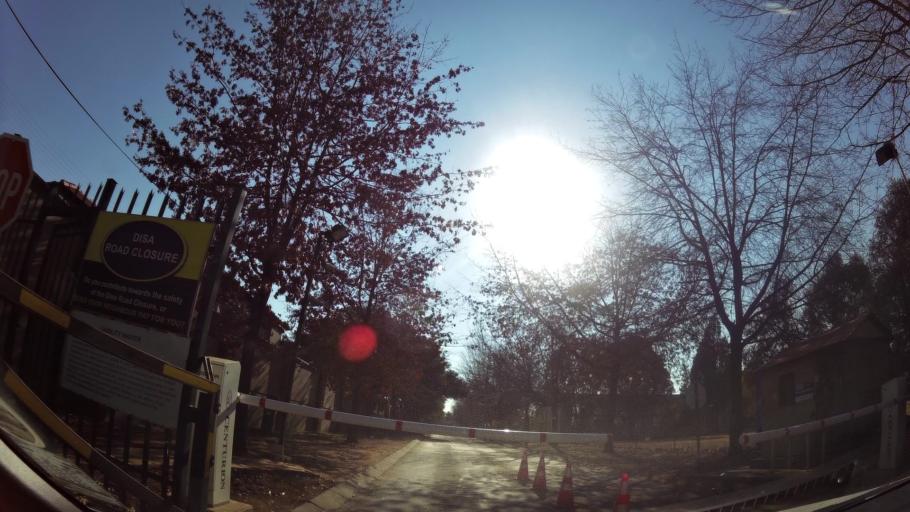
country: ZA
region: Gauteng
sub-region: Ekurhuleni Metropolitan Municipality
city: Germiston
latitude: -26.1703
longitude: 28.1407
